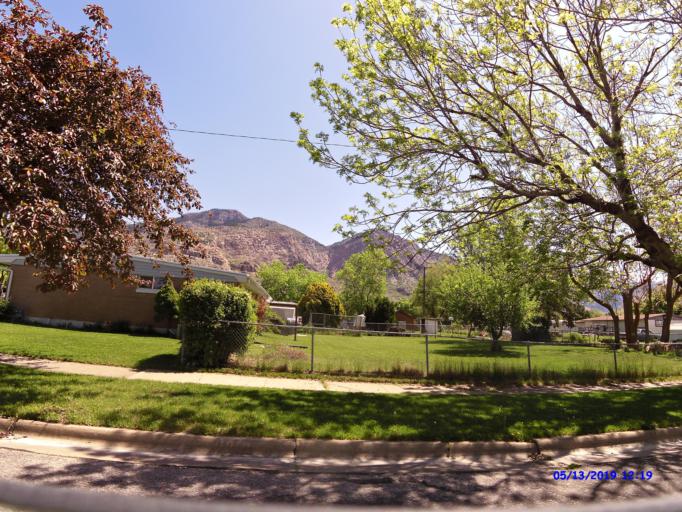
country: US
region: Utah
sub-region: Weber County
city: Harrisville
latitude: 41.2727
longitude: -111.9638
